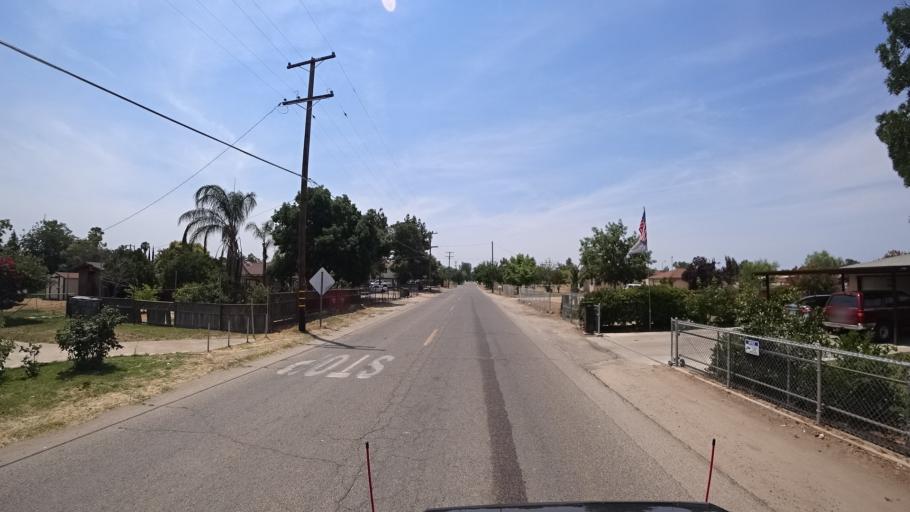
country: US
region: California
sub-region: Fresno County
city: West Park
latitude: 36.7561
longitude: -119.8532
